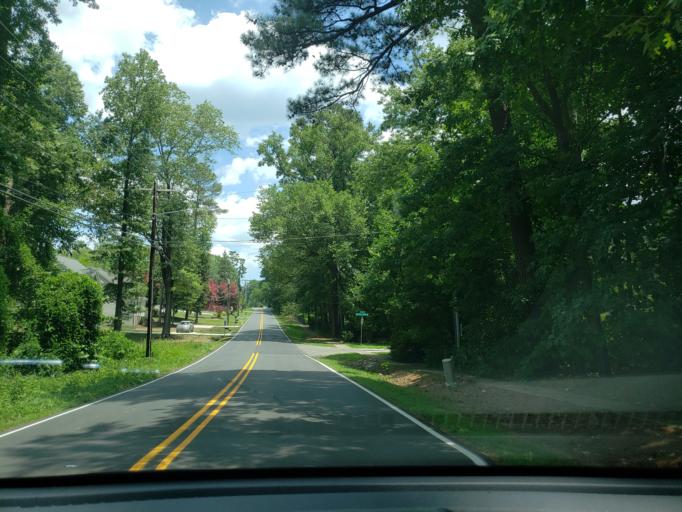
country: US
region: North Carolina
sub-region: Durham County
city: Durham
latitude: 35.9519
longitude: -78.9599
